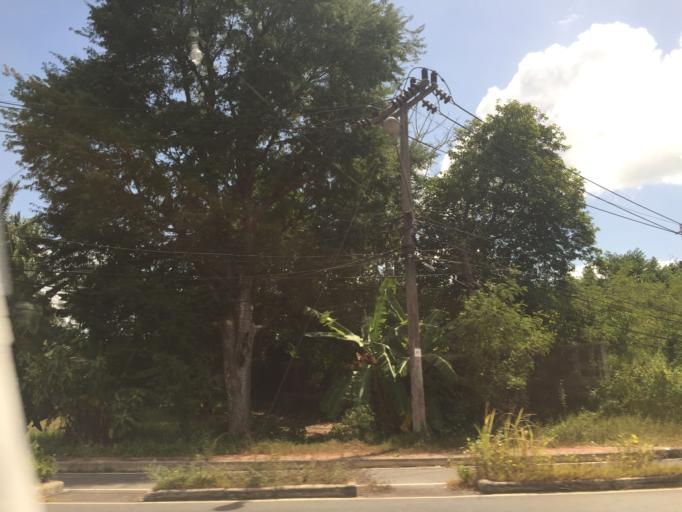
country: TH
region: Phangnga
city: Ban Ao Nang
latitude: 8.0604
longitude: 98.8404
